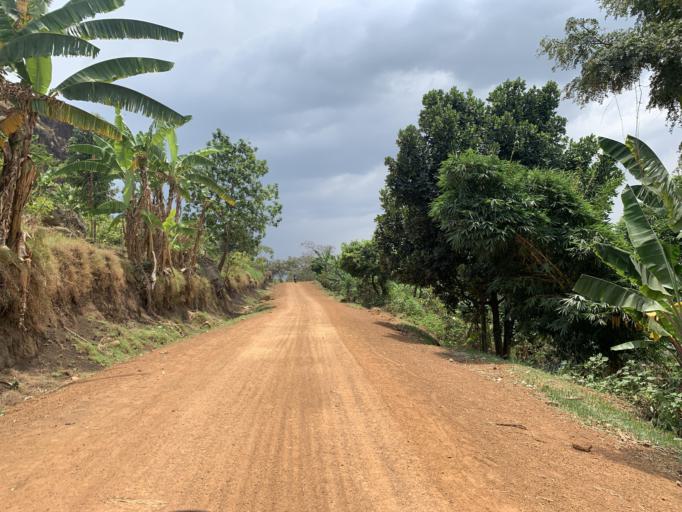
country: UG
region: Eastern Region
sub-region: Sironko District
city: Sironko
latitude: 1.2618
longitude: 34.2977
